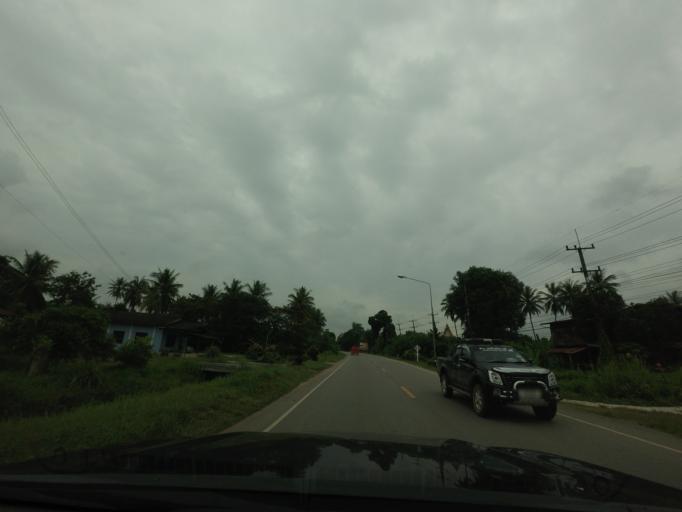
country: TH
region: Nong Khai
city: Si Chiang Mai
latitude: 17.9612
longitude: 102.5296
